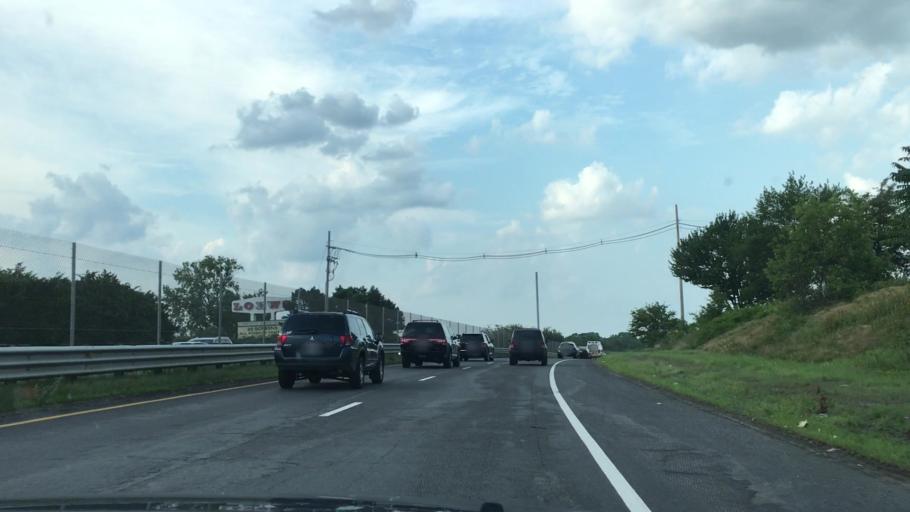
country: US
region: Massachusetts
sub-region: Essex County
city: Danvers
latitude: 42.5521
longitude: -70.9357
